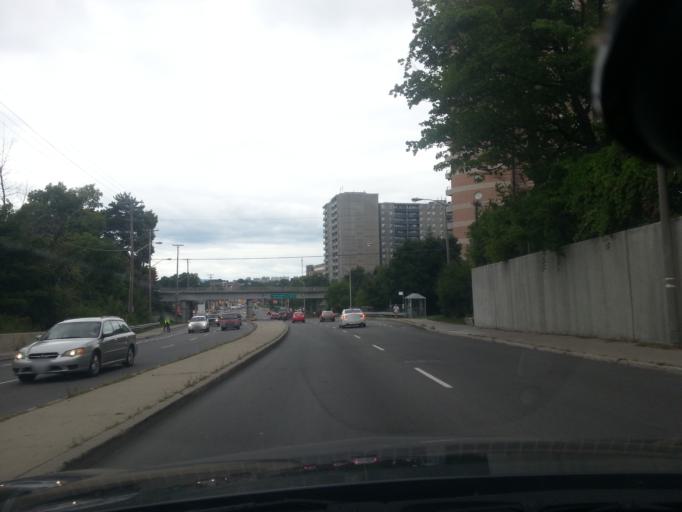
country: CA
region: Ontario
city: Ottawa
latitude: 45.3855
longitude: -75.6730
